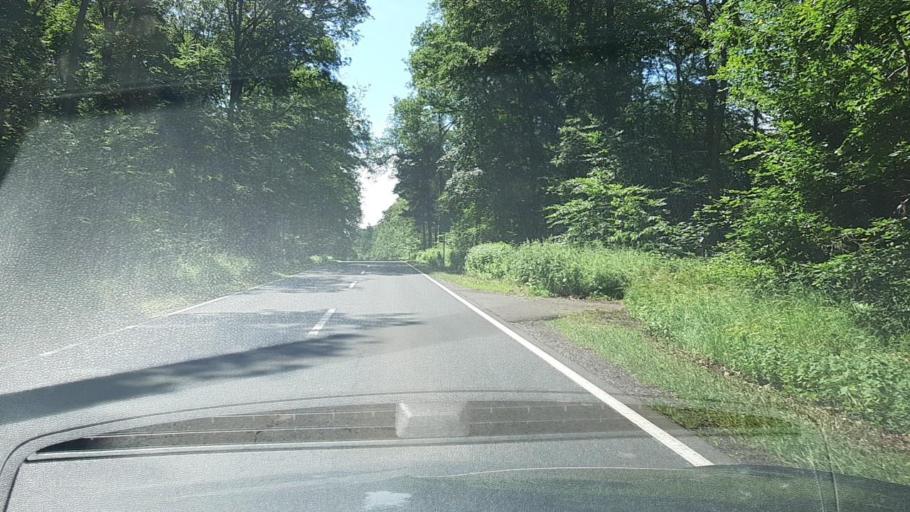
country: DE
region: Rheinland-Pfalz
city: Mesenich
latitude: 50.1081
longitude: 7.1759
